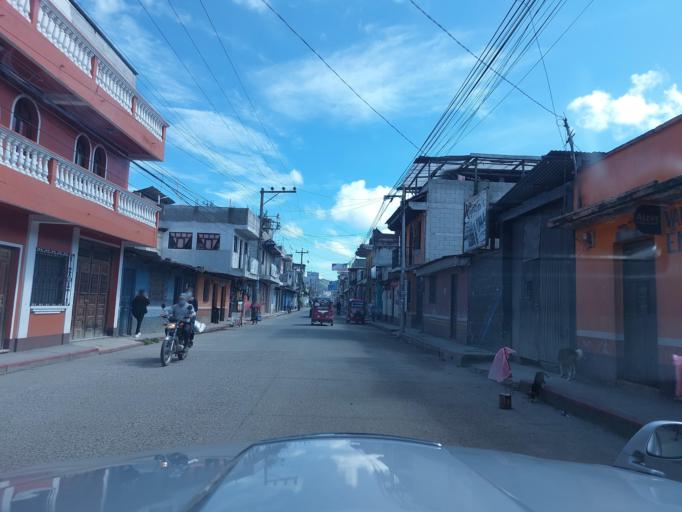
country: GT
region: Chimaltenango
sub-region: Municipio de San Juan Comalapa
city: Comalapa
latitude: 14.7352
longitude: -90.8870
